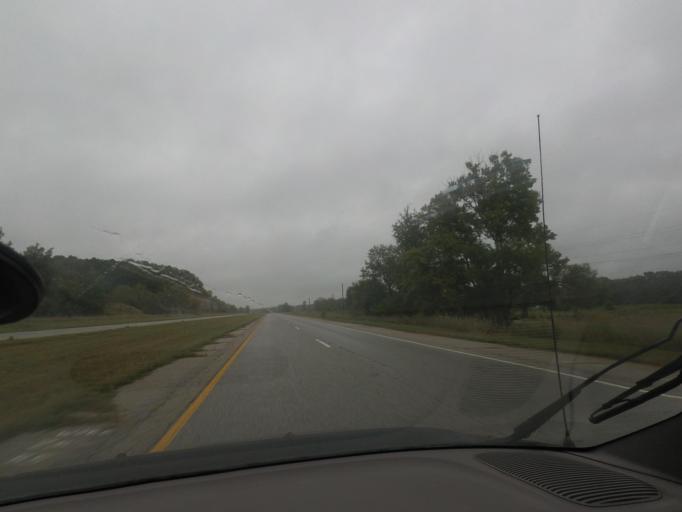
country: US
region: Illinois
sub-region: Pike County
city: Barry
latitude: 39.7134
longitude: -91.0893
